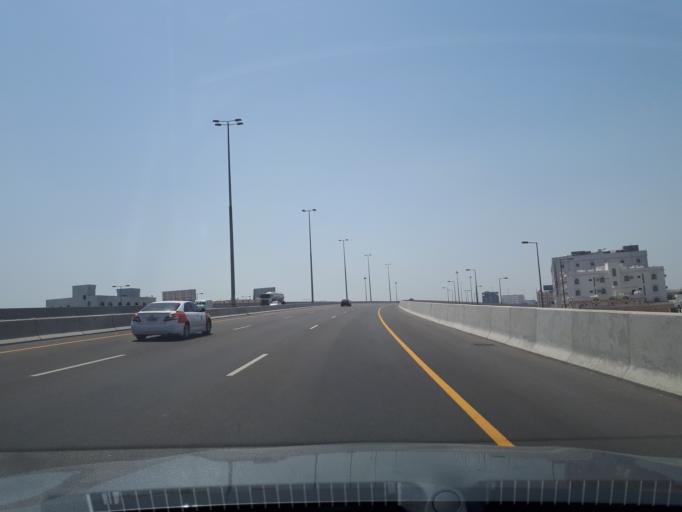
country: OM
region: Al Batinah
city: Al Liwa'
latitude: 24.4225
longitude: 56.6148
